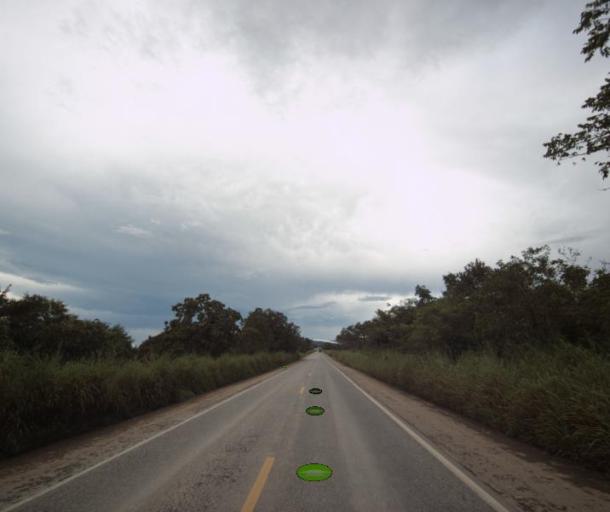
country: BR
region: Goias
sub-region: Porangatu
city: Porangatu
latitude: -13.5664
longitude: -49.0524
